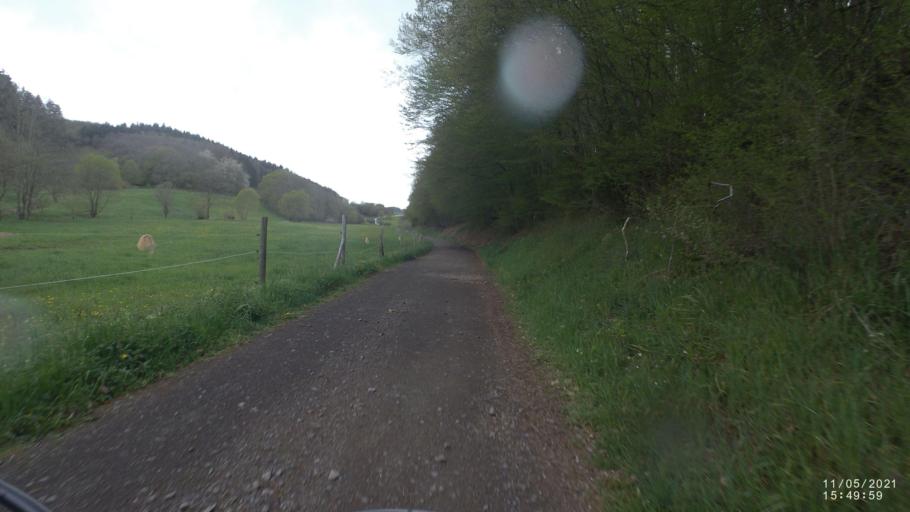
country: DE
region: Rheinland-Pfalz
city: Ditscheid
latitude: 50.3076
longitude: 7.0609
